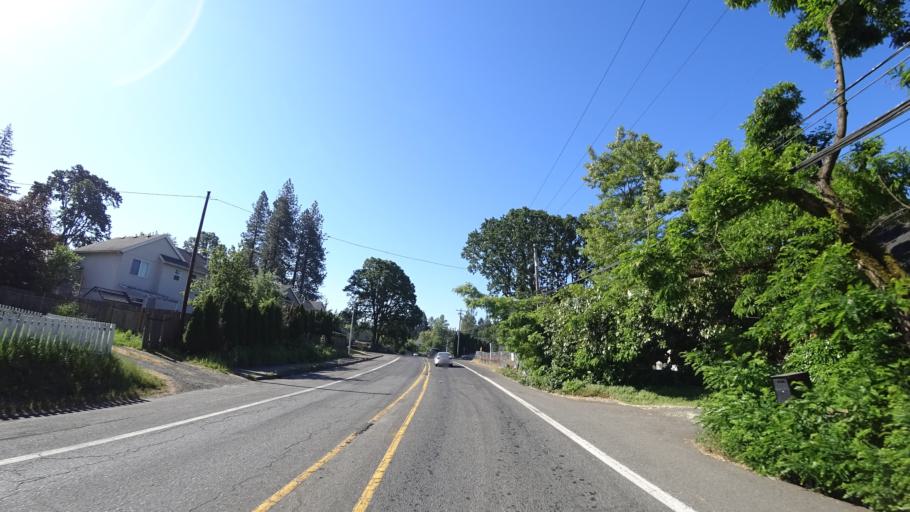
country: US
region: Oregon
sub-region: Washington County
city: Metzger
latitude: 45.4428
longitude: -122.7657
